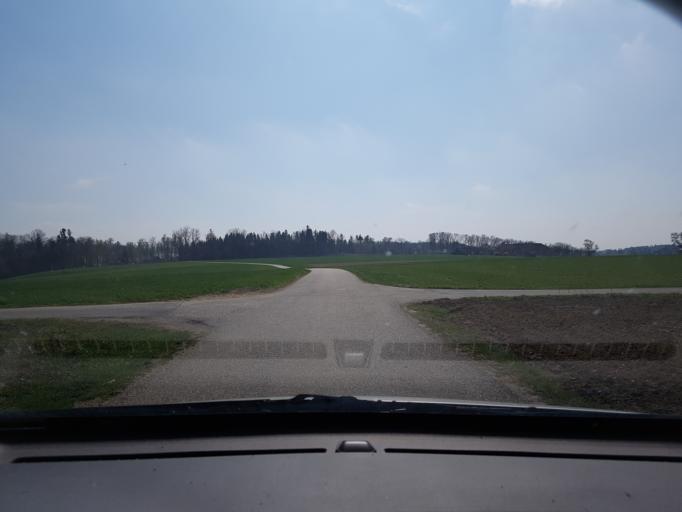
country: AT
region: Upper Austria
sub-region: Politischer Bezirk Linz-Land
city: Ansfelden
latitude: 48.1697
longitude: 14.3209
